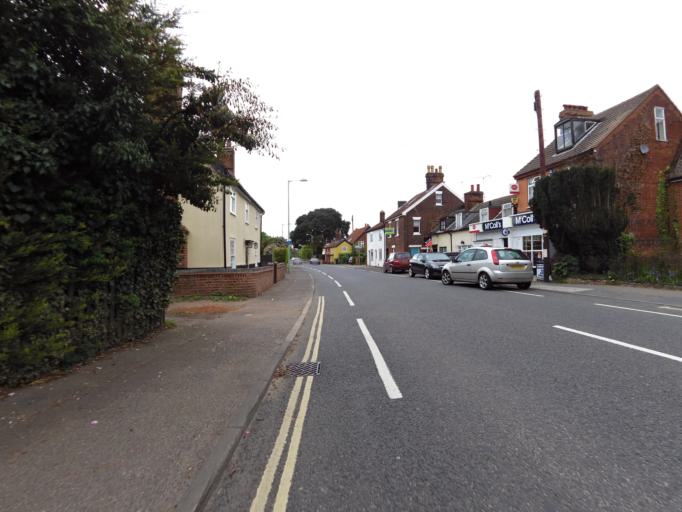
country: GB
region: England
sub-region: Suffolk
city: Felixstowe
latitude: 51.9853
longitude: 1.3137
